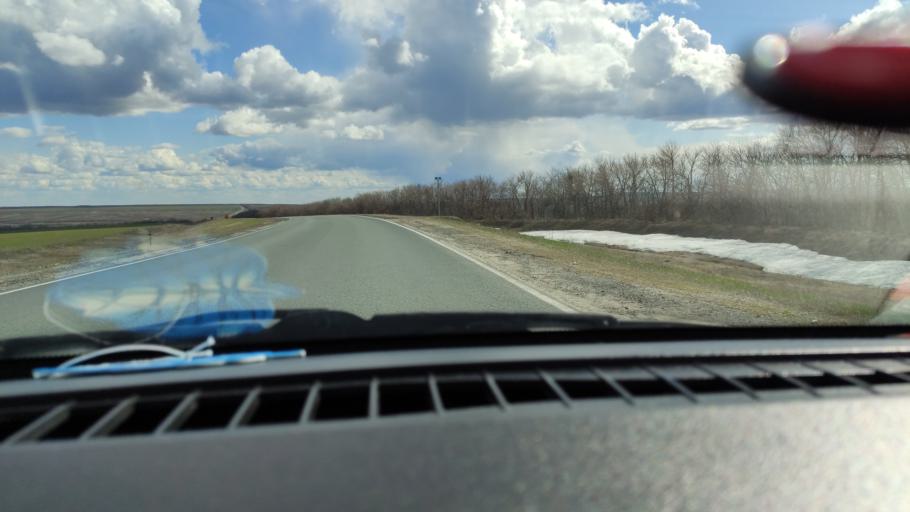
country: RU
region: Saratov
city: Dukhovnitskoye
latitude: 52.7631
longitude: 48.2399
